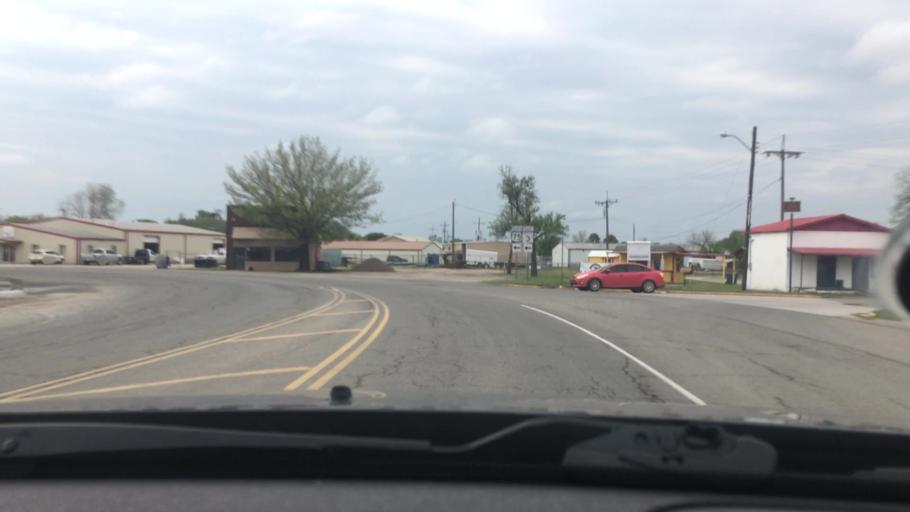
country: US
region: Oklahoma
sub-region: Coal County
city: Coalgate
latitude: 34.5373
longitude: -96.2187
